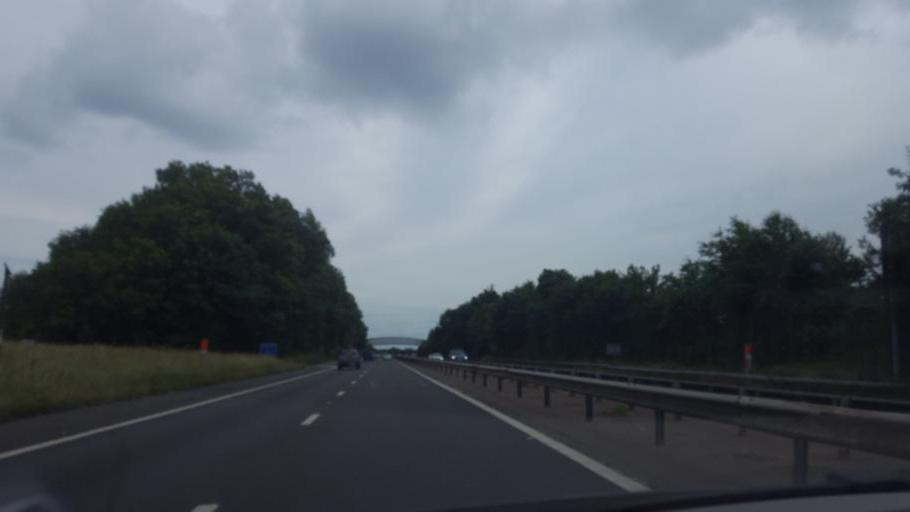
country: GB
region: England
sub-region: Royal Borough of Windsor and Maidenhead
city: Maidenhead
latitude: 51.5068
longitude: -0.7346
